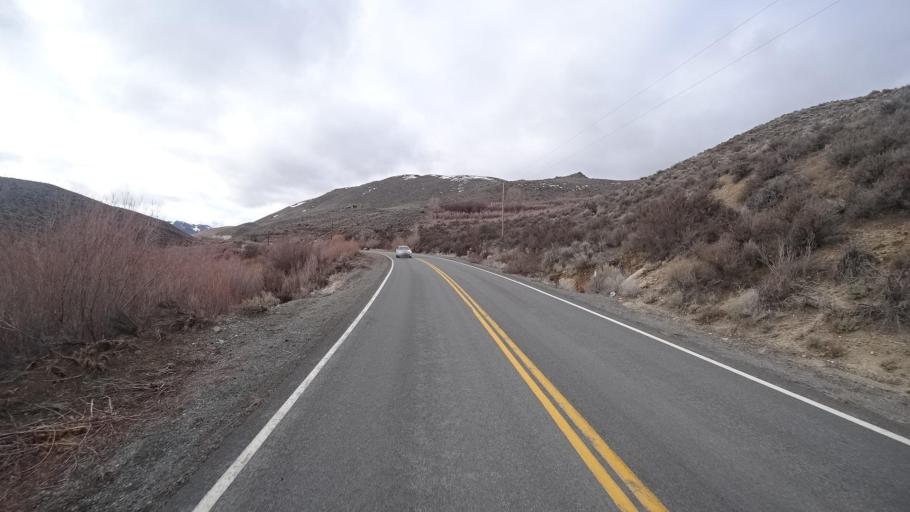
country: US
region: Nevada
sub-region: Washoe County
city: Cold Springs
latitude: 39.8306
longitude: -119.9384
